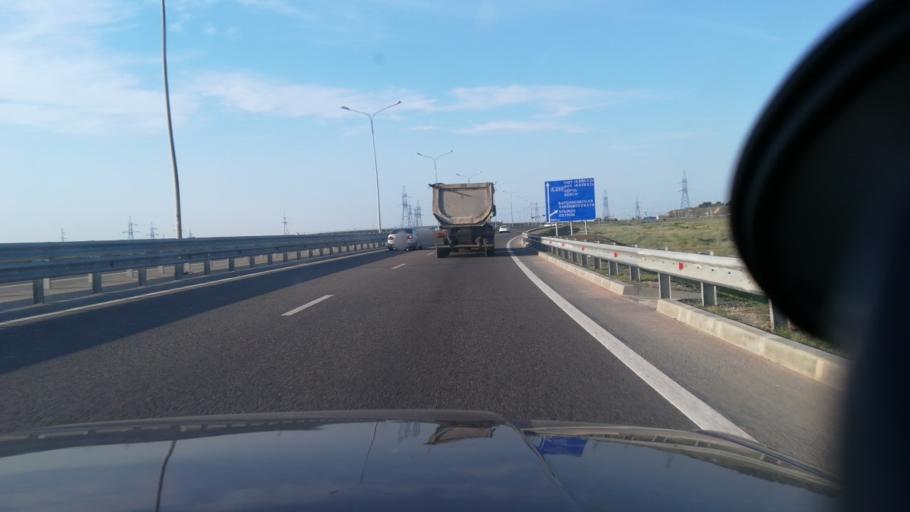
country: RU
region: Krasnodarskiy
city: Dzhiginka
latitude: 45.1311
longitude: 37.3123
